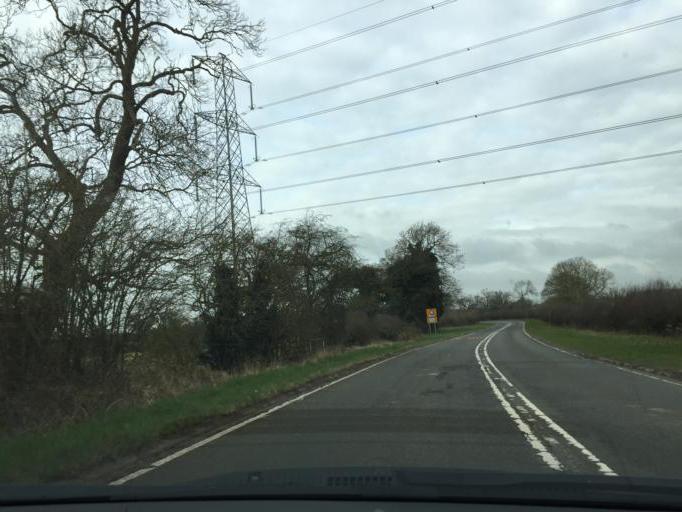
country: GB
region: England
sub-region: Warwickshire
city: Henley in Arden
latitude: 52.2906
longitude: -1.8120
